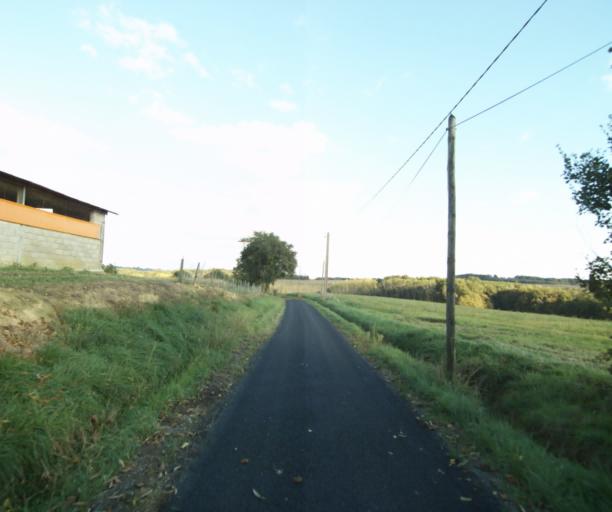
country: FR
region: Midi-Pyrenees
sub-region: Departement du Gers
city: Eauze
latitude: 43.7474
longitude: 0.1419
